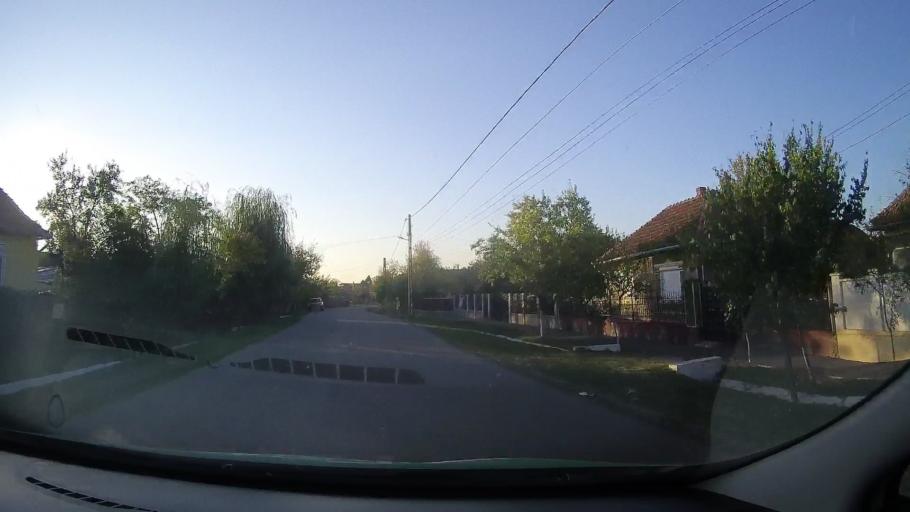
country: RO
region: Bihor
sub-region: Comuna Salard
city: Salard
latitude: 47.2231
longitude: 22.0339
